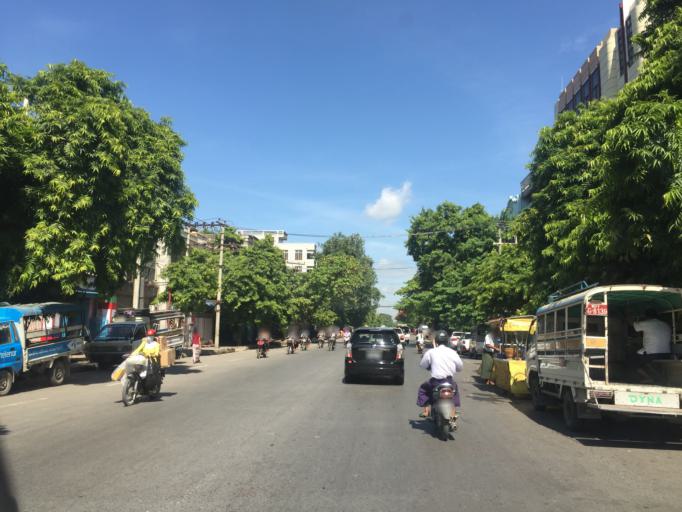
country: MM
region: Mandalay
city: Mandalay
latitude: 21.9837
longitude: 96.0755
